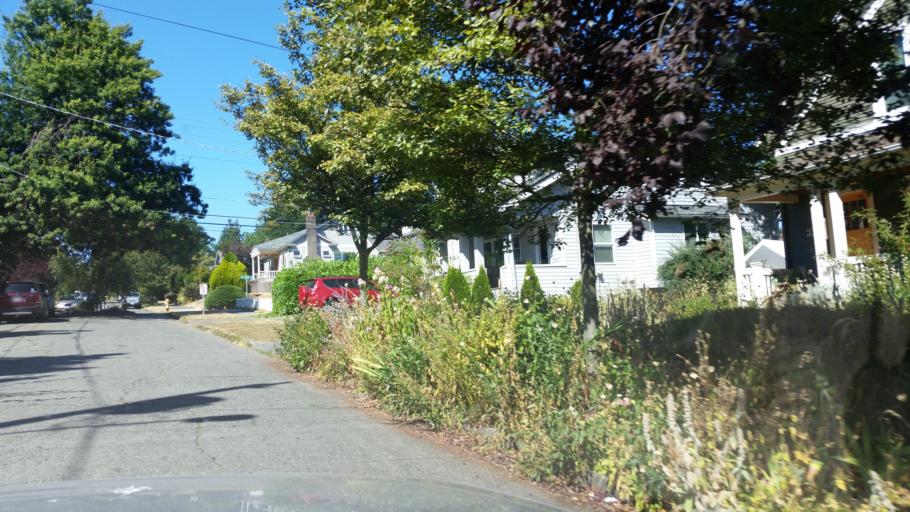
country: US
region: Washington
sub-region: King County
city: Seattle
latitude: 47.6585
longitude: -122.3273
